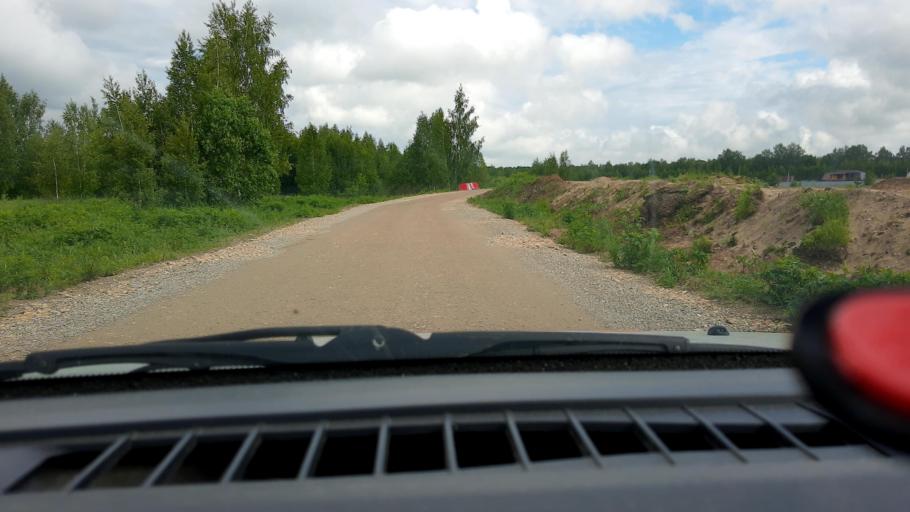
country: RU
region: Nizjnij Novgorod
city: Neklyudovo
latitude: 56.4281
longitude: 43.9627
